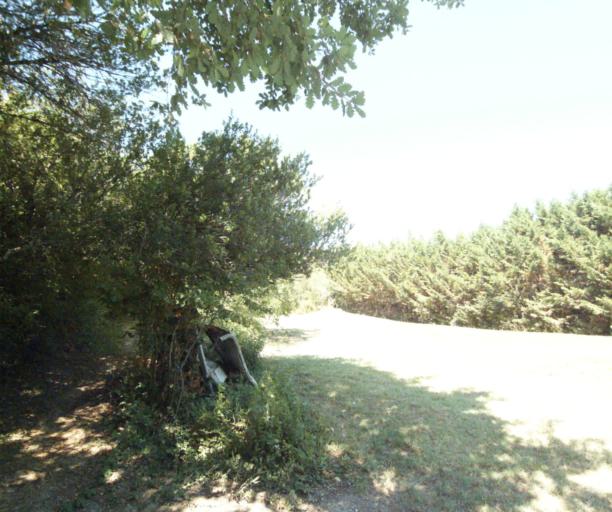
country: FR
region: Midi-Pyrenees
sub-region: Departement de la Haute-Garonne
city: Saint-Felix-Lauragais
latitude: 43.4884
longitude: 1.8964
